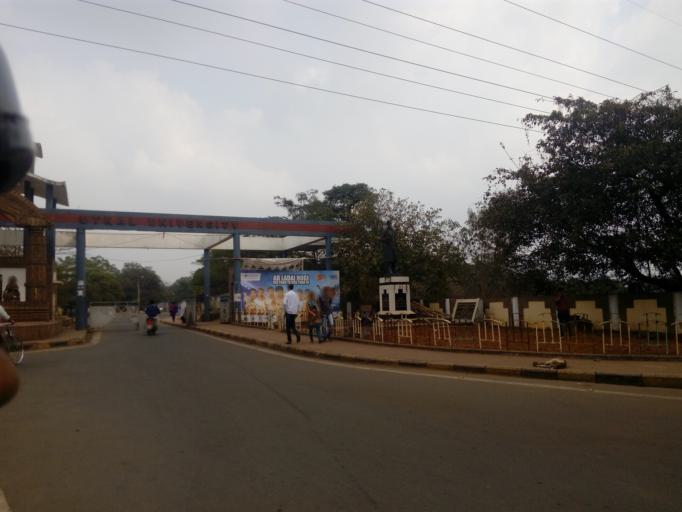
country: IN
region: Odisha
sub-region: Khordha
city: Bhubaneshwar
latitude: 20.2968
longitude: 85.8405
